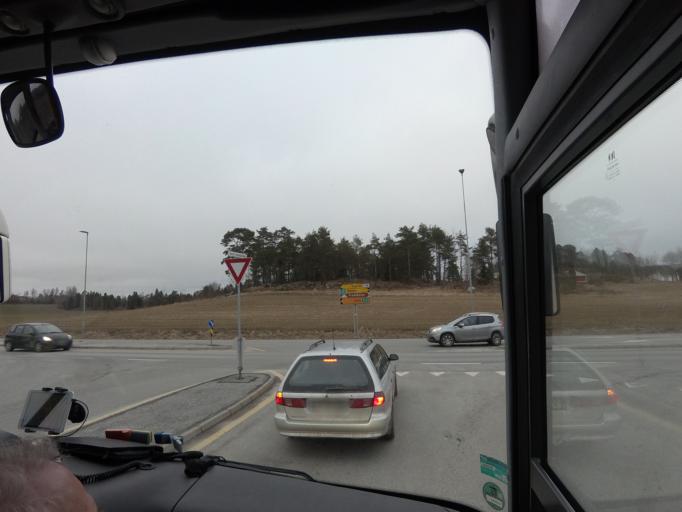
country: NO
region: Ostfold
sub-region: Halden
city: Halden
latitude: 59.1222
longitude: 11.2818
